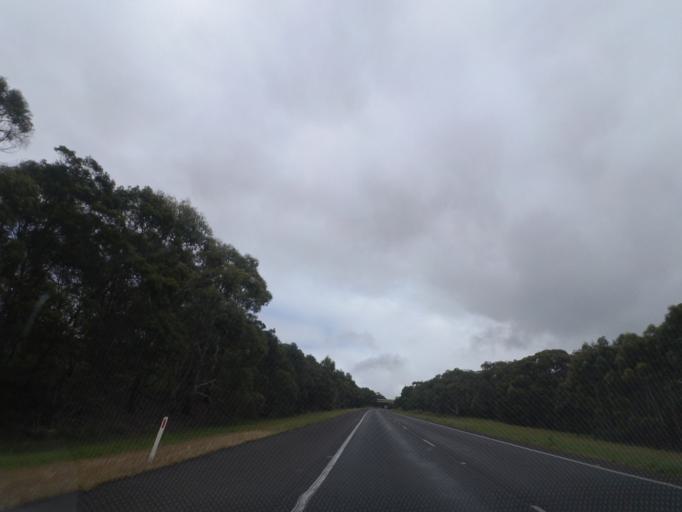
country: AU
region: Victoria
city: Brown Hill
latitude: -37.5404
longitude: 143.8841
